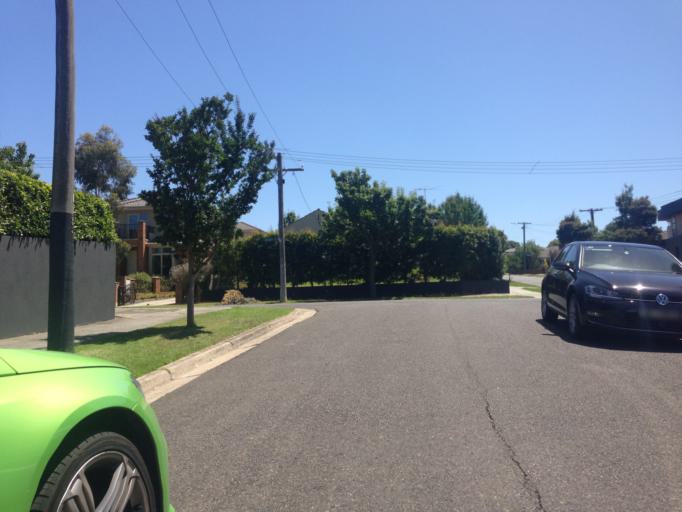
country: AU
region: Victoria
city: Balwyn
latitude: -37.7981
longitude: 145.0738
